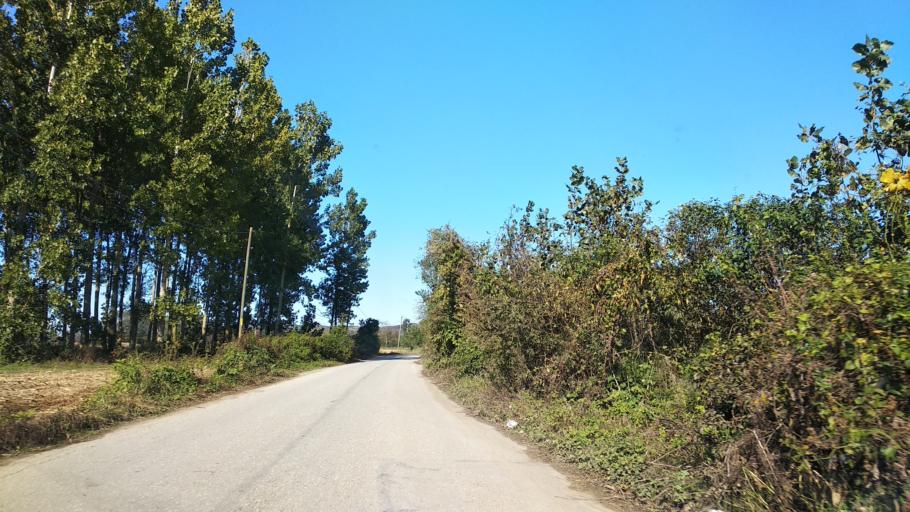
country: TR
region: Sakarya
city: Ortakoy
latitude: 41.0308
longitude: 30.6076
